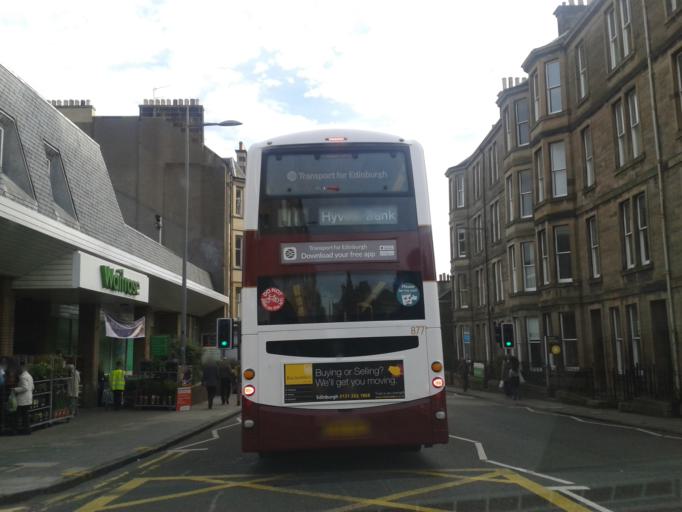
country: GB
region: Scotland
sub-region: Edinburgh
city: Edinburgh
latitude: 55.9301
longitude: -3.2097
